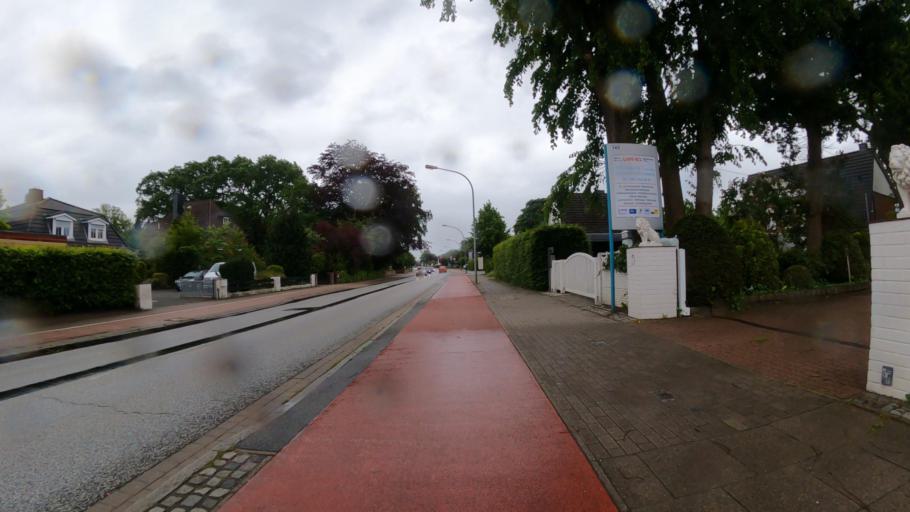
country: DE
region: Schleswig-Holstein
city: Norderstedt
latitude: 53.6949
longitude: 9.9940
